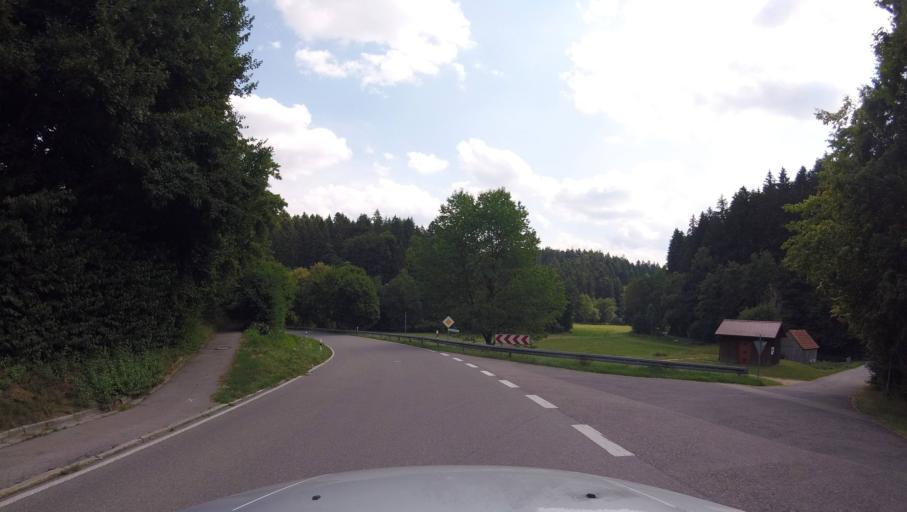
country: DE
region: Baden-Wuerttemberg
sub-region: Regierungsbezirk Stuttgart
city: Alfdorf
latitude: 48.8909
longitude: 9.7009
